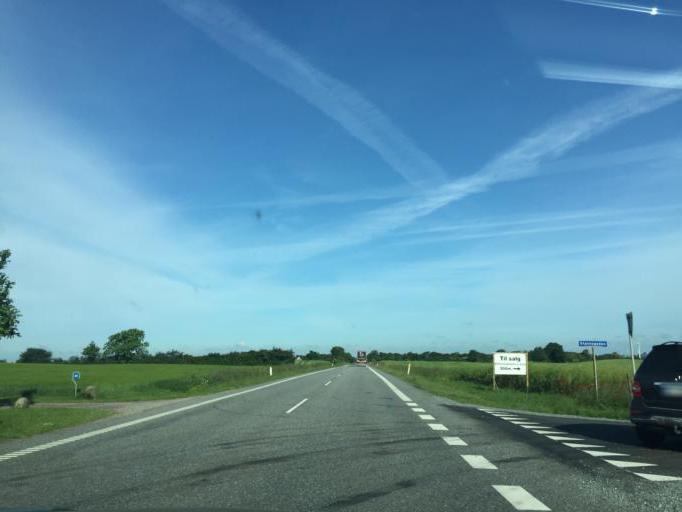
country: DK
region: South Denmark
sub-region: Middelfart Kommune
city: Ejby
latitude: 55.4585
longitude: 9.9418
